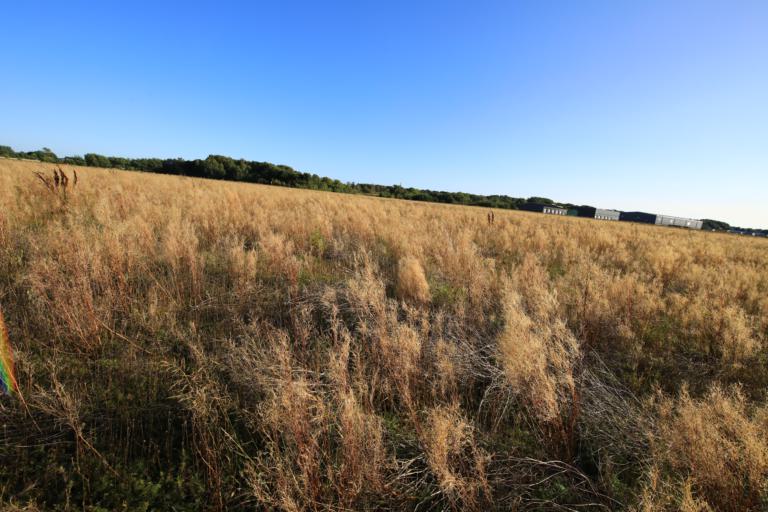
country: SE
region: Halland
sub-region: Varbergs Kommun
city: Varberg
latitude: 57.1232
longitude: 12.3067
